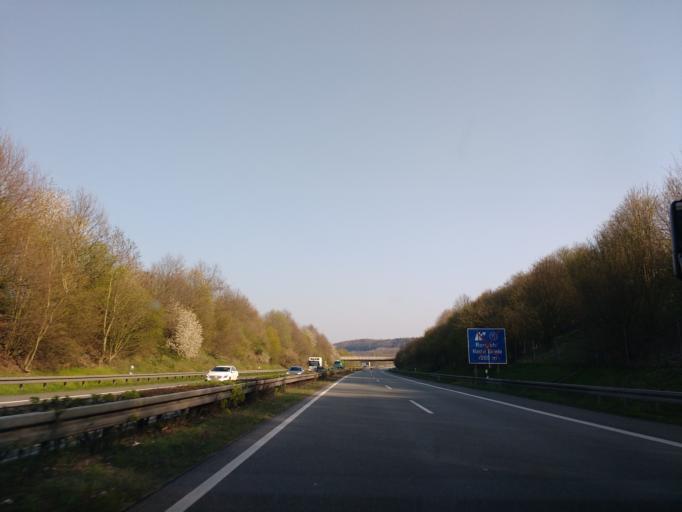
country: DE
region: Lower Saxony
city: Bissendorf
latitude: 52.2099
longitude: 8.1283
